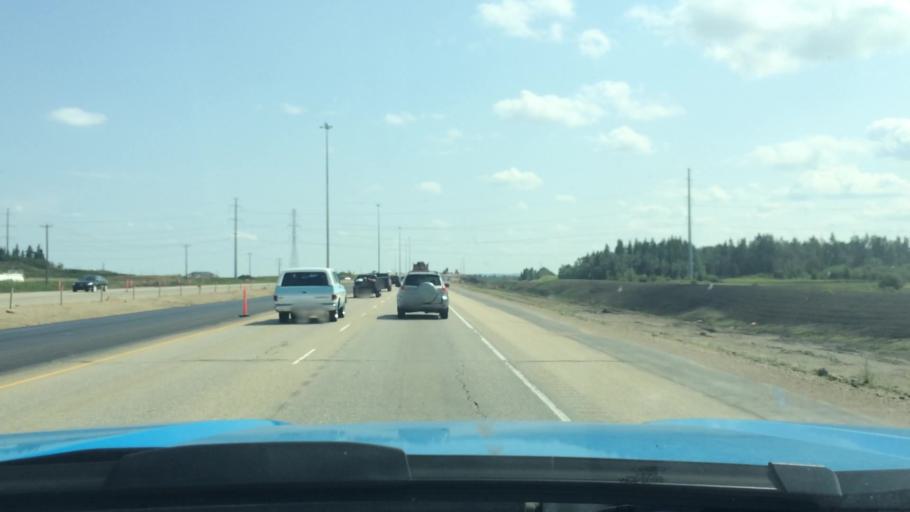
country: CA
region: Alberta
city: Red Deer
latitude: 52.2397
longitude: -113.8318
